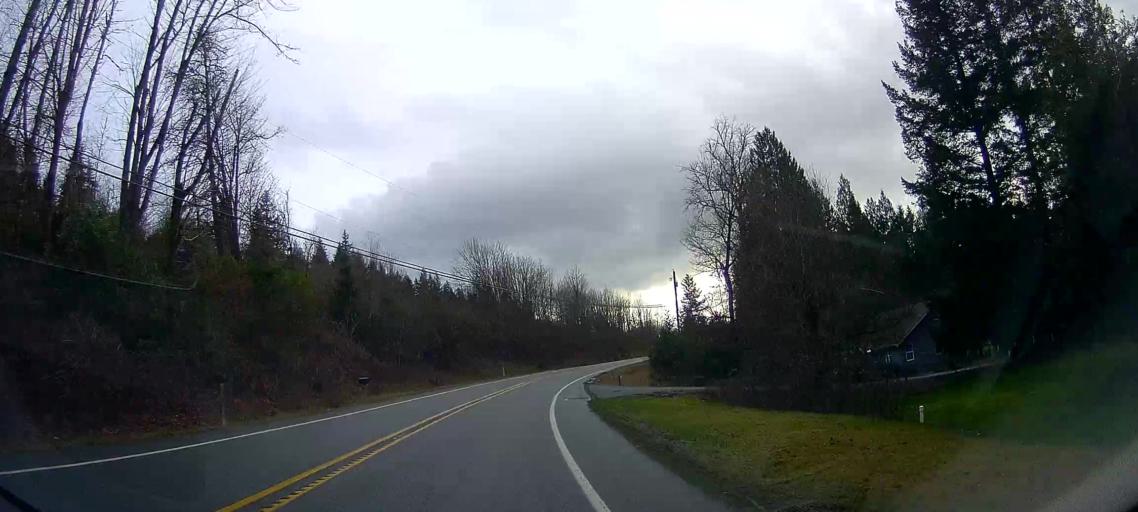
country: US
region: Washington
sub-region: Skagit County
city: Sedro-Woolley
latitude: 48.5965
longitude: -122.2298
